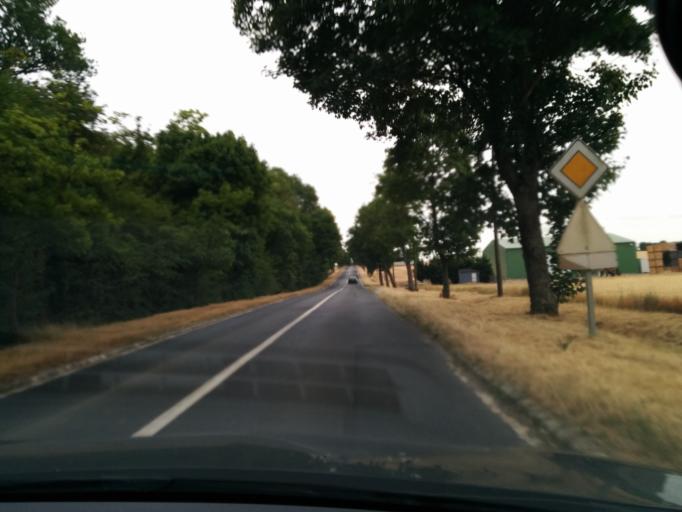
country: FR
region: Ile-de-France
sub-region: Departement de l'Essonne
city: Pussay
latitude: 48.3461
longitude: 1.9877
